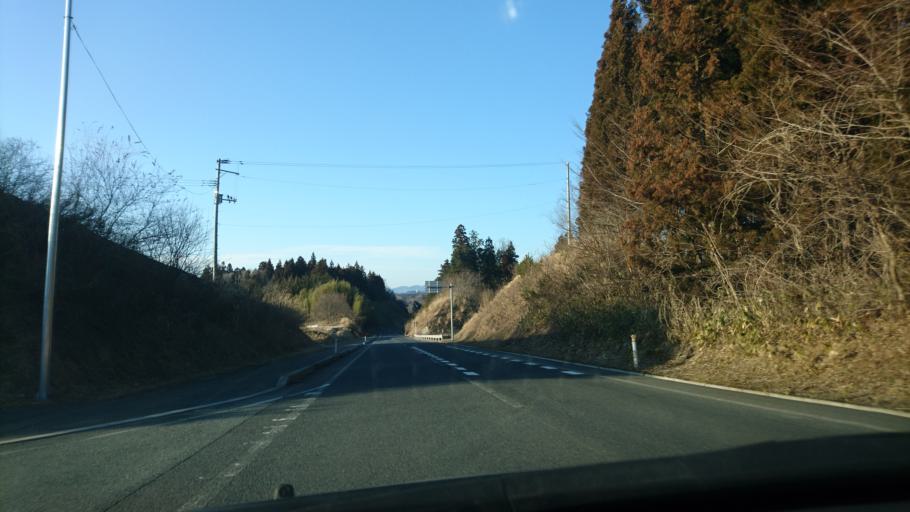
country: JP
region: Iwate
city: Ichinoseki
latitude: 38.9249
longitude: 141.3628
